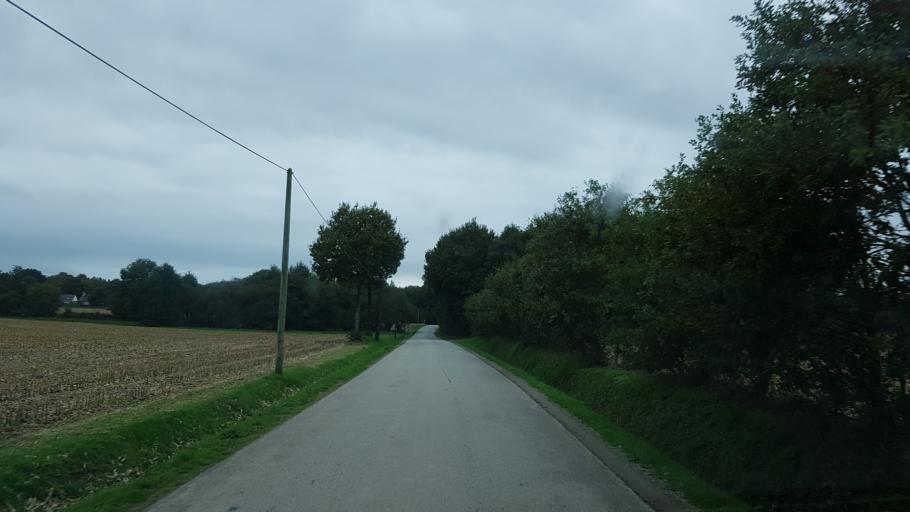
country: FR
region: Brittany
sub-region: Departement du Morbihan
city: Serent
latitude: 47.7803
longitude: -2.4709
